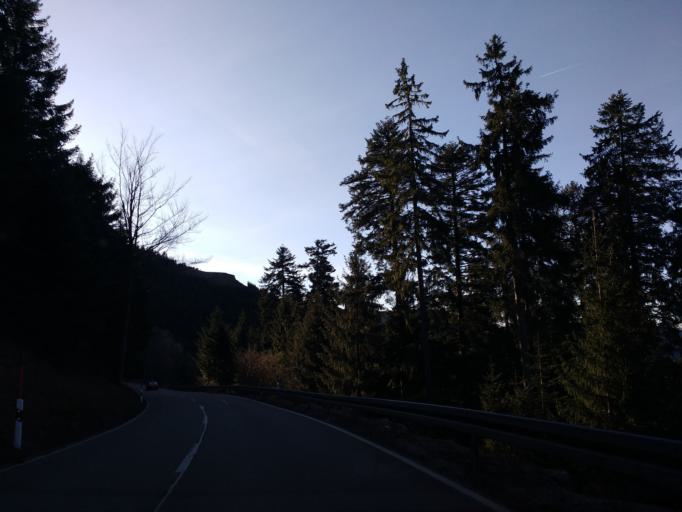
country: DE
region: Baden-Wuerttemberg
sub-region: Freiburg Region
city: Bad Peterstal-Griesbach
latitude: 48.4625
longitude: 8.2601
